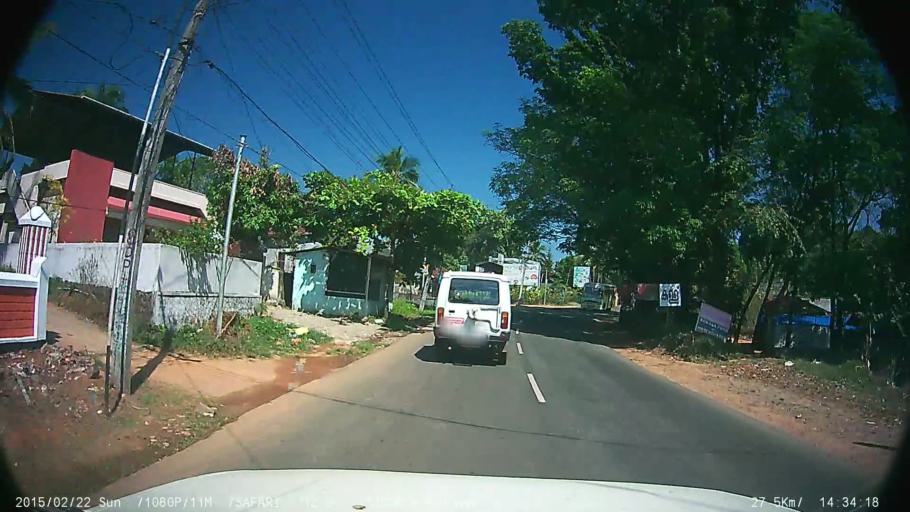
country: IN
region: Kerala
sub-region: Kottayam
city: Erattupetta
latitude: 9.5631
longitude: 76.7746
